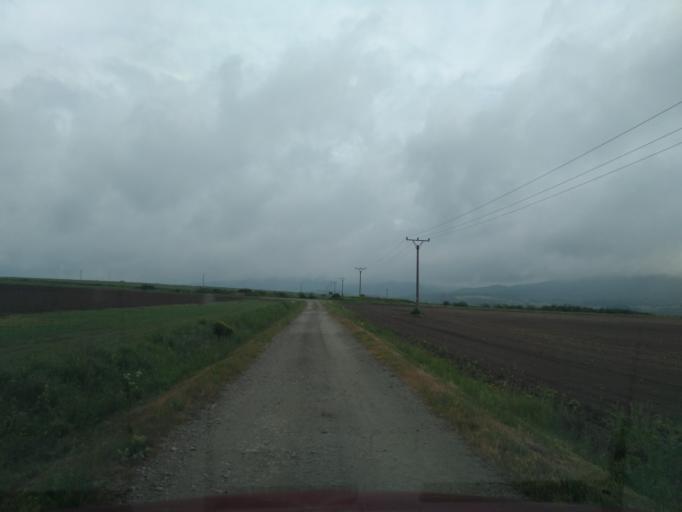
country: SK
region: Kosicky
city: Secovce
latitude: 48.7640
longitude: 21.4724
